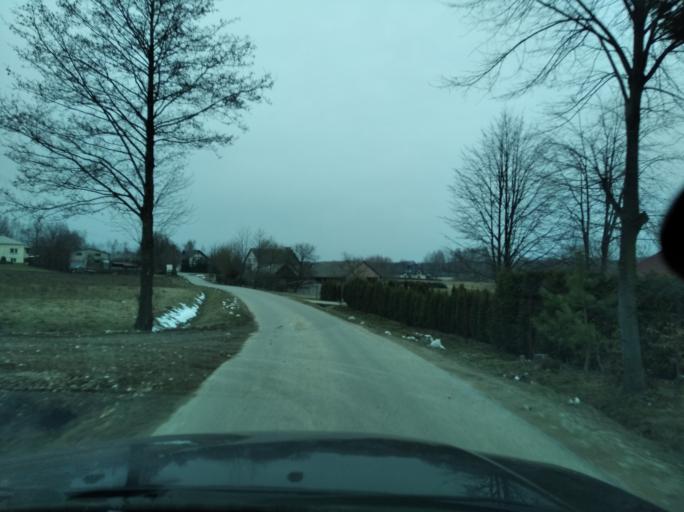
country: PL
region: Subcarpathian Voivodeship
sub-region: Powiat rzeszowski
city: Chmielnik
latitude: 49.9905
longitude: 22.1458
